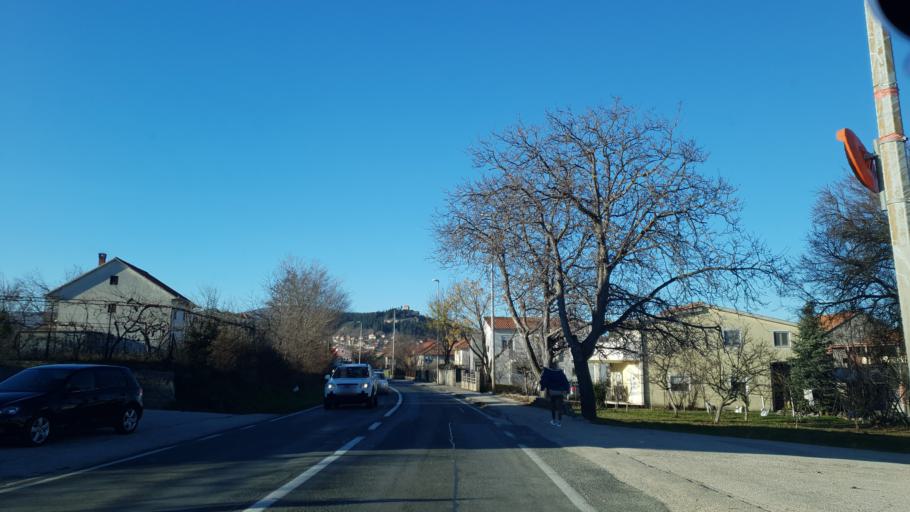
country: HR
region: Splitsko-Dalmatinska
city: Sinj
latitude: 43.6921
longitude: 16.6449
